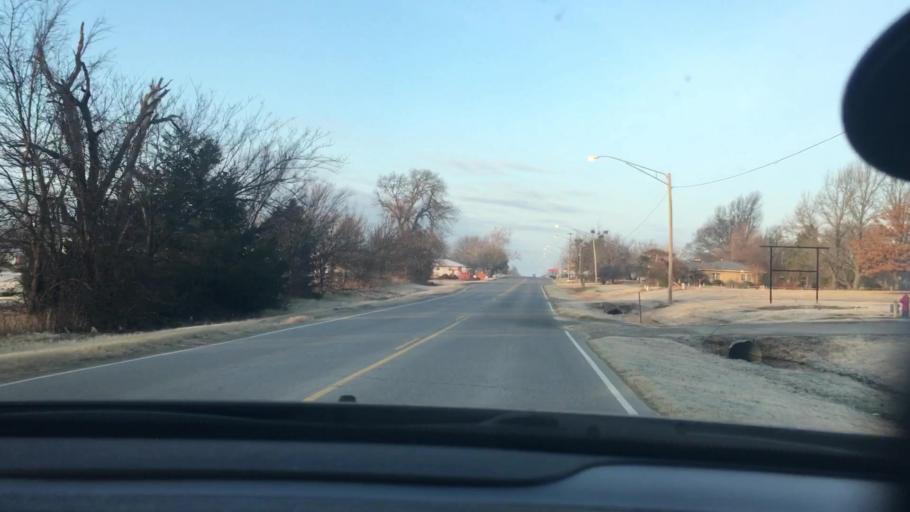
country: US
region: Oklahoma
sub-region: Garvin County
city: Stratford
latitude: 34.7970
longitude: -96.9478
